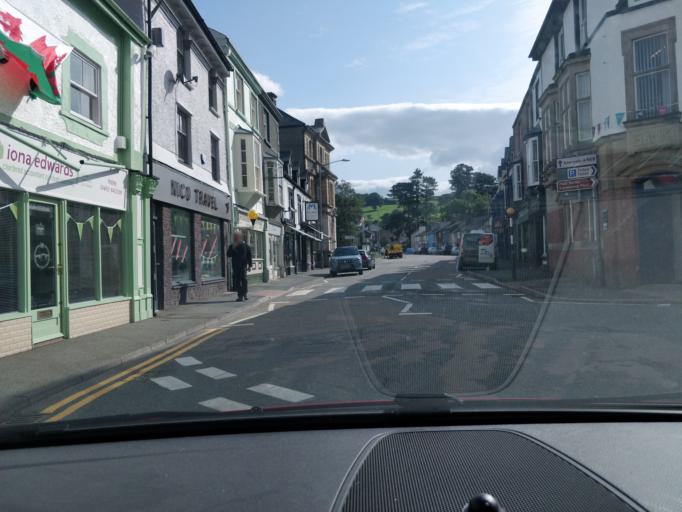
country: GB
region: Wales
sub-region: Conwy
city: Llanrwst
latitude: 53.1389
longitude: -3.7973
